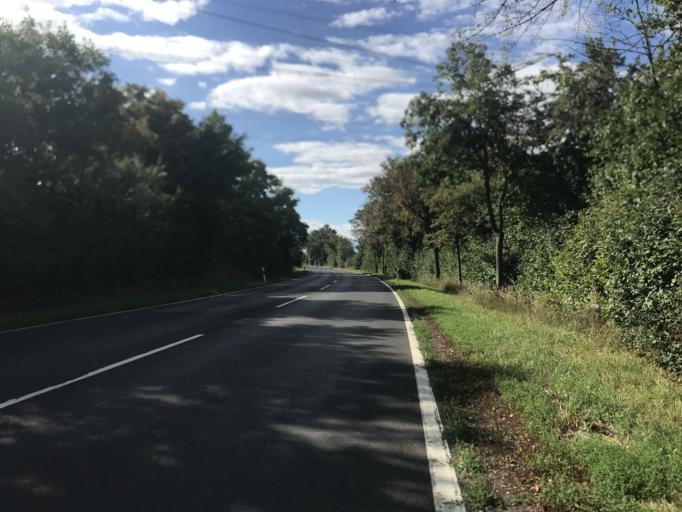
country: DE
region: Hesse
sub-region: Regierungsbezirk Darmstadt
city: Bischofsheim
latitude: 50.0058
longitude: 8.3828
